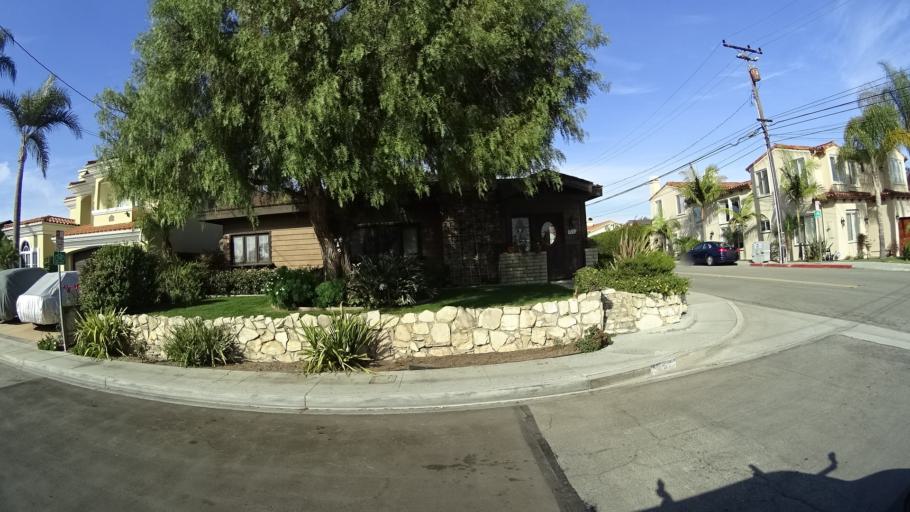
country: US
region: California
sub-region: Los Angeles County
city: Hermosa Beach
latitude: 33.8738
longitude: -118.3832
